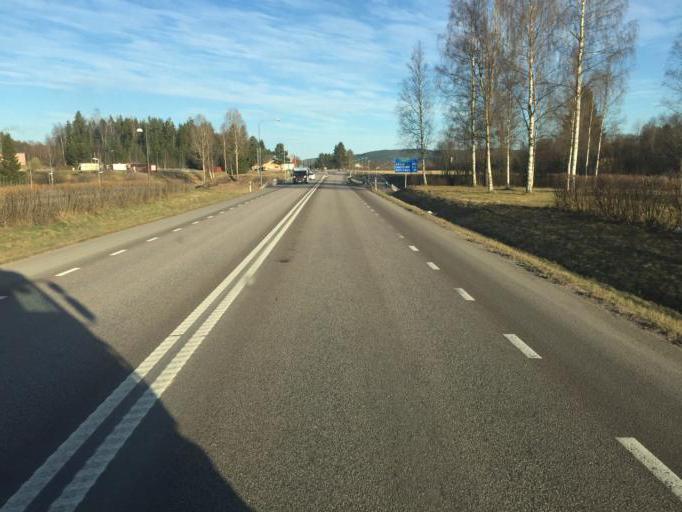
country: SE
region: Dalarna
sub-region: Gagnefs Kommun
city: Djuras
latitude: 60.5594
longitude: 15.1365
